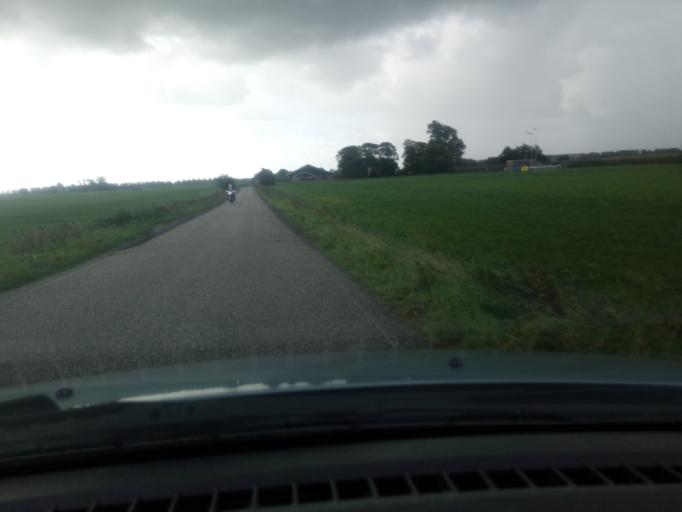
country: NL
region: Groningen
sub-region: Gemeente Grootegast
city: Grootegast
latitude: 53.2560
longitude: 6.2472
